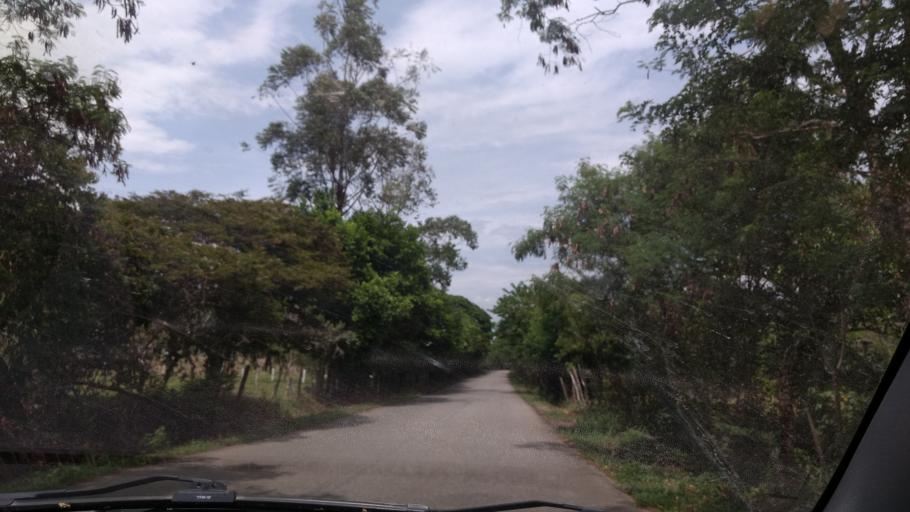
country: CO
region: Cauca
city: Buenos Aires
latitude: 3.0672
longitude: -76.6555
